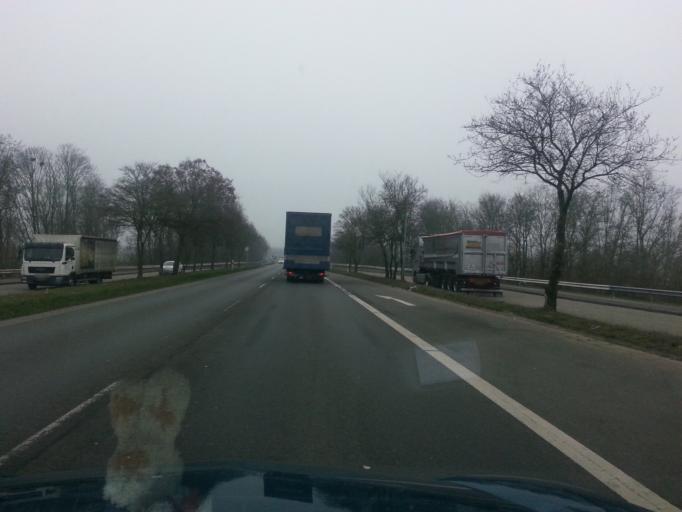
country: DE
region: North Rhine-Westphalia
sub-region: Regierungsbezirk Dusseldorf
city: Emmerich
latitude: 51.8334
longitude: 6.2268
